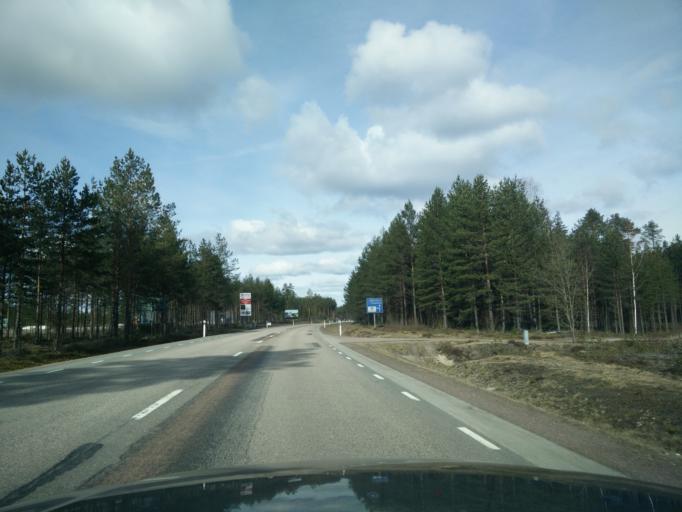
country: SE
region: Vaermland
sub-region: Hagfors Kommun
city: Hagfors
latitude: 60.0225
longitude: 13.5902
